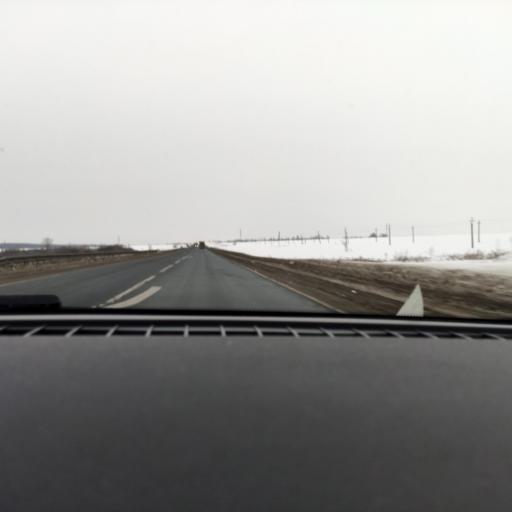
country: RU
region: Samara
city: Smyshlyayevka
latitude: 53.2876
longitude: 50.4608
